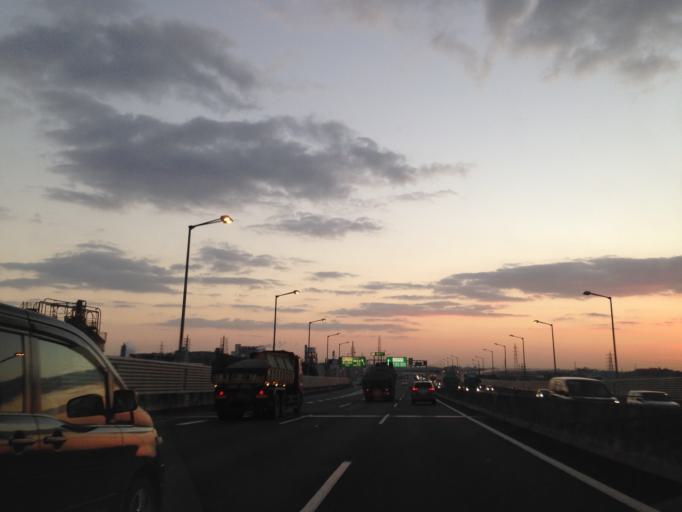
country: JP
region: Aichi
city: Obu
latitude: 35.0521
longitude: 136.8890
